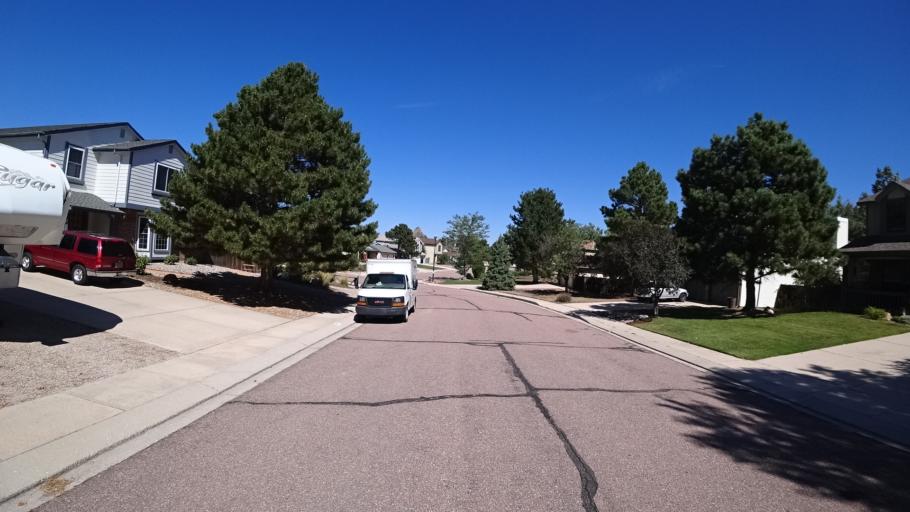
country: US
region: Colorado
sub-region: El Paso County
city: Black Forest
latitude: 38.9502
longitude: -104.7494
